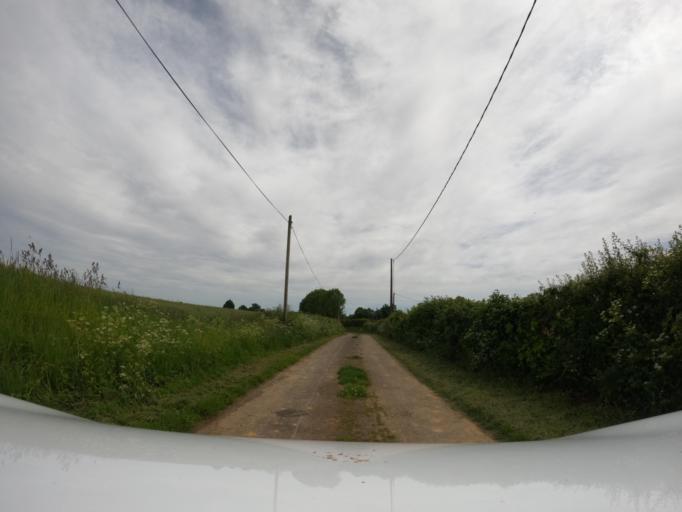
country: FR
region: Pays de la Loire
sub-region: Departement de la Vendee
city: Saint-Hilaire-des-Loges
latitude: 46.4889
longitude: -0.6290
